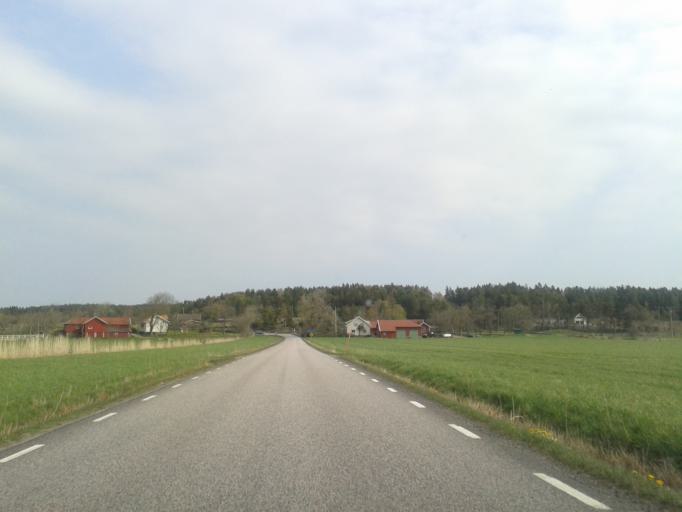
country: SE
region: Vaestra Goetaland
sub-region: Kungalvs Kommun
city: Kode
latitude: 57.9137
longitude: 11.8024
